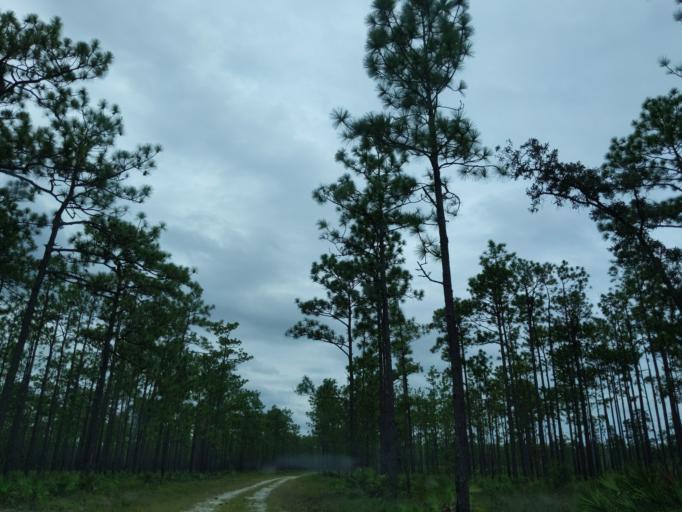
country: US
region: Florida
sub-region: Gadsden County
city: Midway
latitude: 30.3563
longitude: -84.4867
